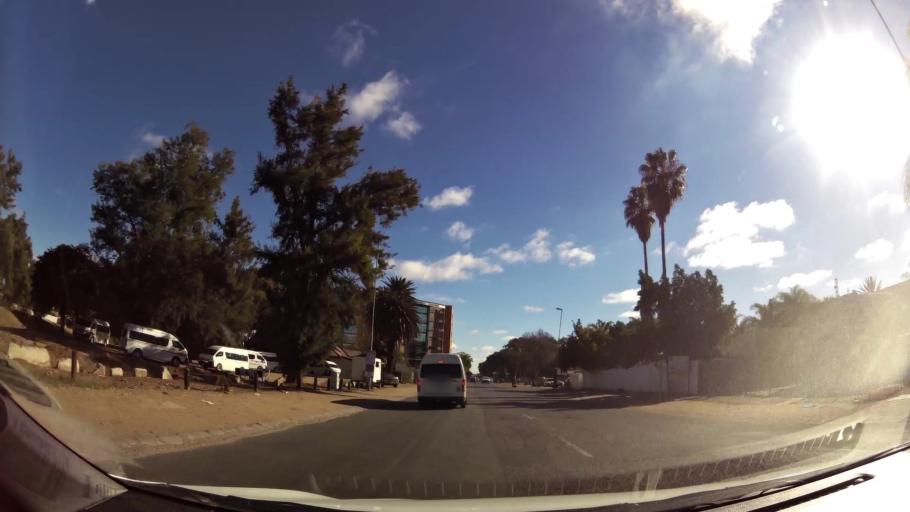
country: ZA
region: Limpopo
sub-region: Capricorn District Municipality
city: Polokwane
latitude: -23.9154
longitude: 29.4510
